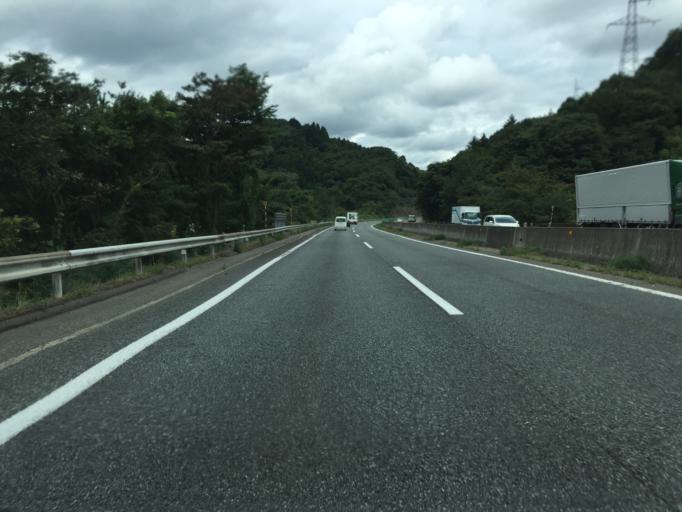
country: JP
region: Fukushima
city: Yanagawamachi-saiwaicho
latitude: 37.9165
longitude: 140.6026
